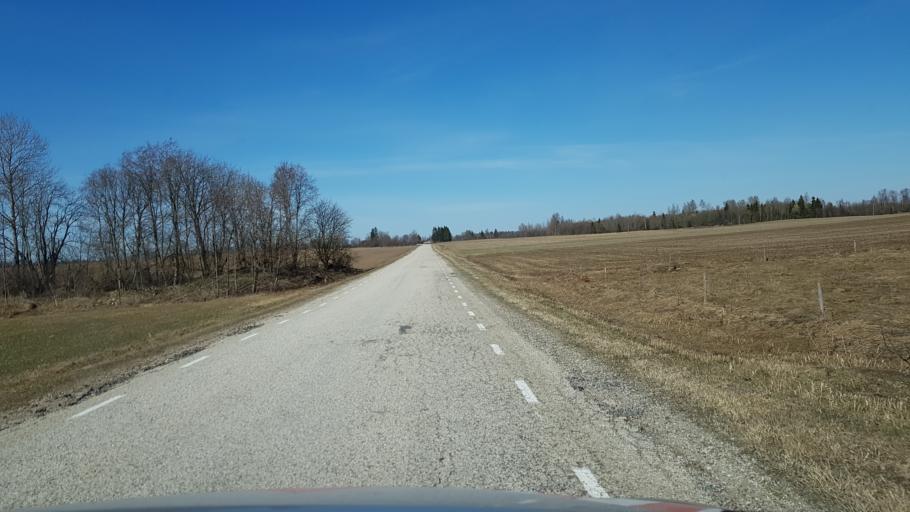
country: EE
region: Laeaene-Virumaa
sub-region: Vinni vald
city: Vinni
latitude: 59.0795
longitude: 26.5483
